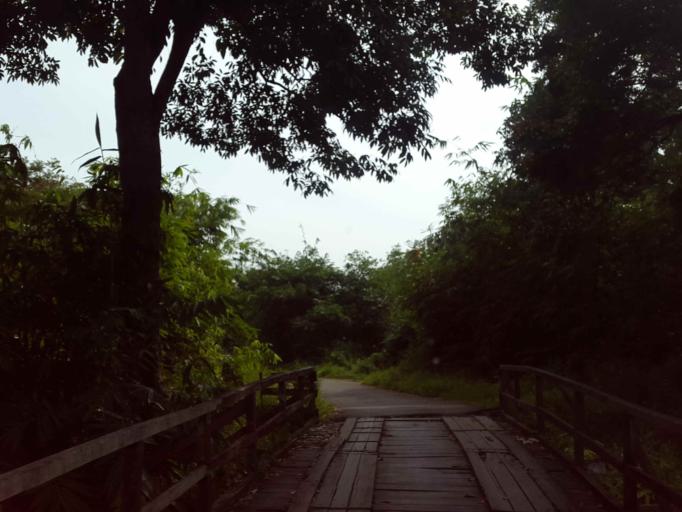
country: MY
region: Sarawak
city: Kuching
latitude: 0.8660
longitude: 110.4423
